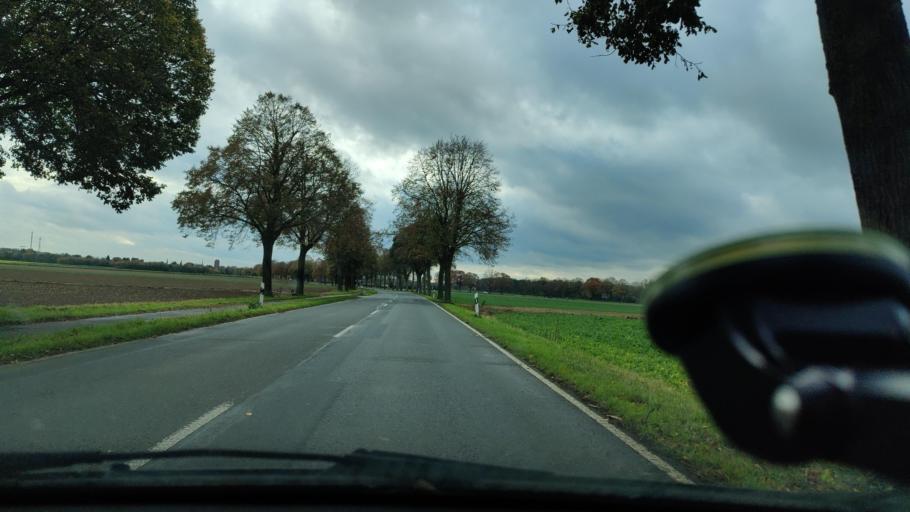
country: DE
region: North Rhine-Westphalia
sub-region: Regierungsbezirk Dusseldorf
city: Uedem
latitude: 51.6835
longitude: 6.2691
